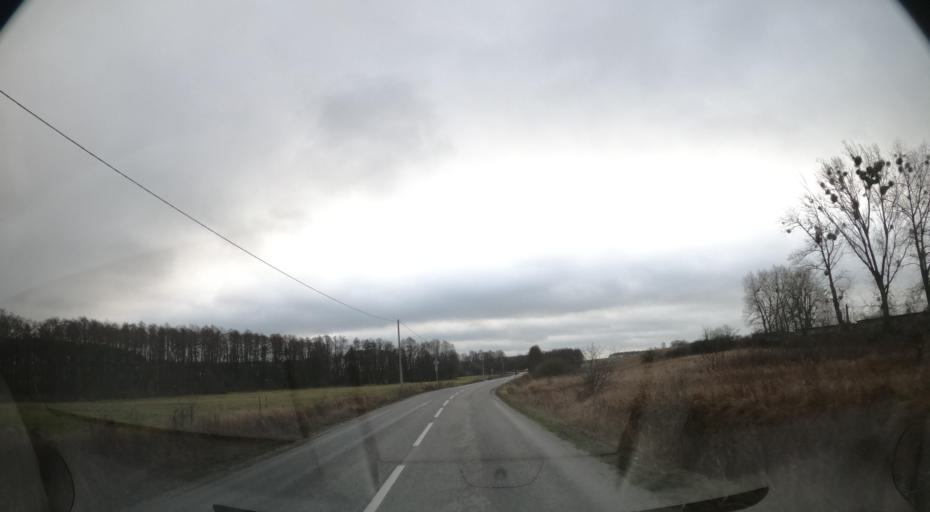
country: PL
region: Kujawsko-Pomorskie
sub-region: Powiat nakielski
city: Sadki
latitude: 53.1905
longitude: 17.3936
